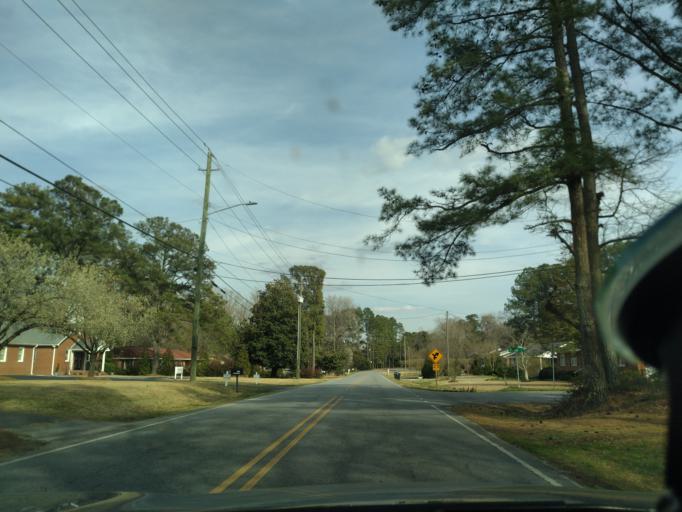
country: US
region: North Carolina
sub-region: Pitt County
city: Greenville
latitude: 35.5931
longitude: -77.3508
